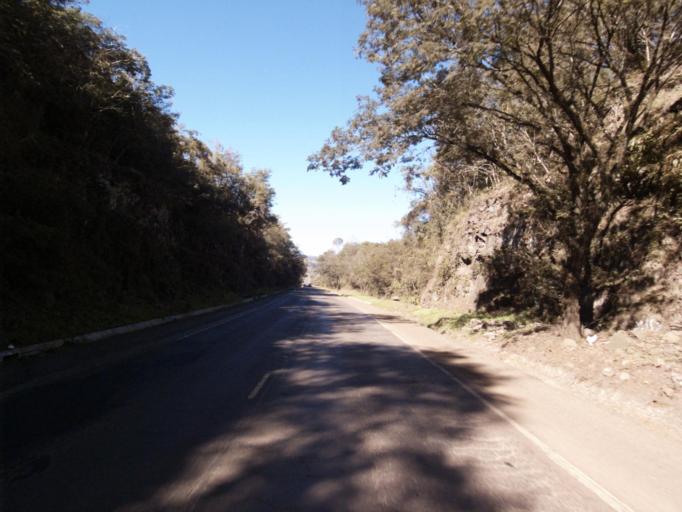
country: BR
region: Santa Catarina
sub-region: Sao Lourenco Do Oeste
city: Sao Lourenco dOeste
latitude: -26.7928
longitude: -53.1944
